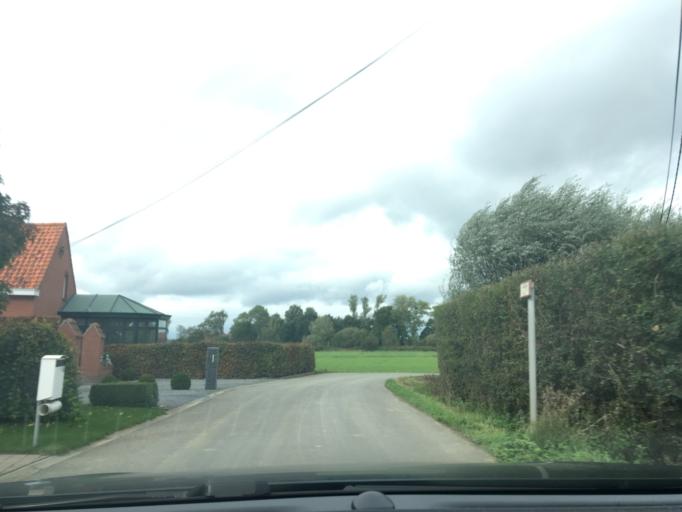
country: BE
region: Flanders
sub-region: Provincie West-Vlaanderen
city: Moorslede
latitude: 50.8989
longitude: 3.0490
